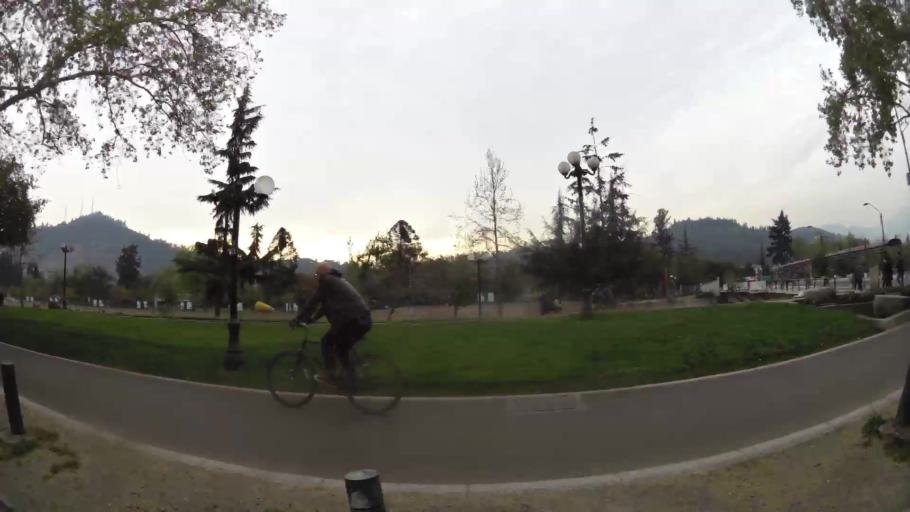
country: CL
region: Santiago Metropolitan
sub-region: Provincia de Santiago
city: Villa Presidente Frei, Nunoa, Santiago, Chile
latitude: -33.4204
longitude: -70.6115
